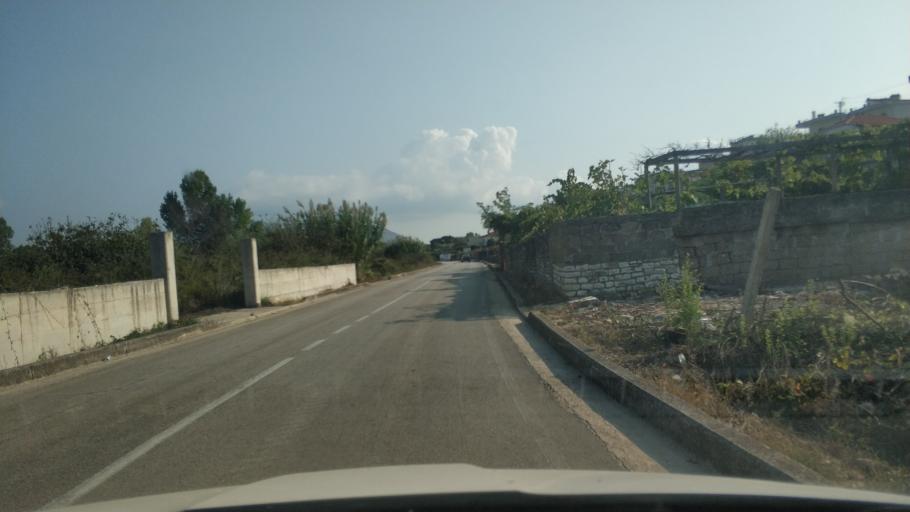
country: AL
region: Vlore
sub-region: Rrethi i Sarandes
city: Sarande
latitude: 39.8455
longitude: 20.0368
